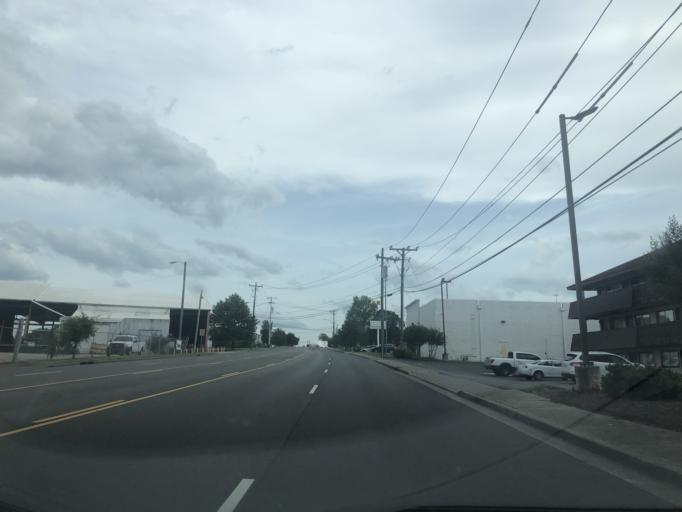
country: US
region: Tennessee
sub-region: Davidson County
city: Oak Hill
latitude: 36.0865
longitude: -86.7621
